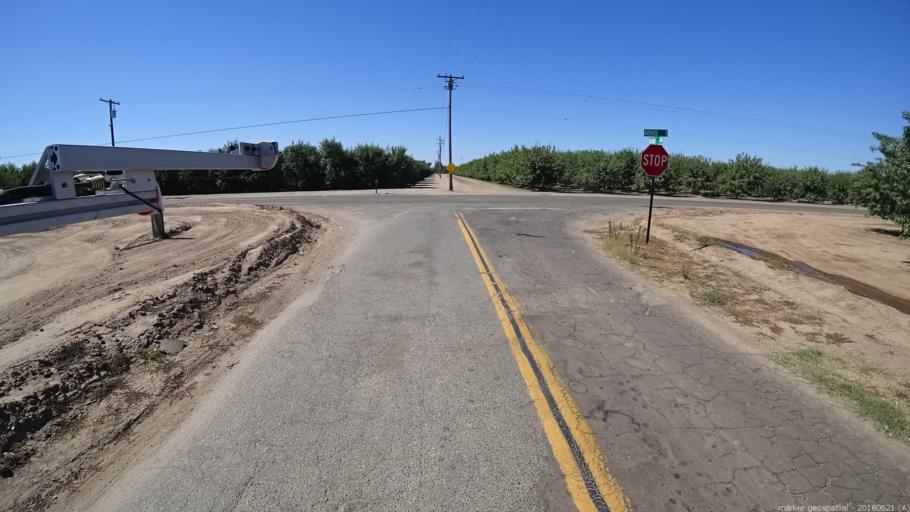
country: US
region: California
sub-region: Fresno County
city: Biola
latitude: 36.8516
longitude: -119.9292
